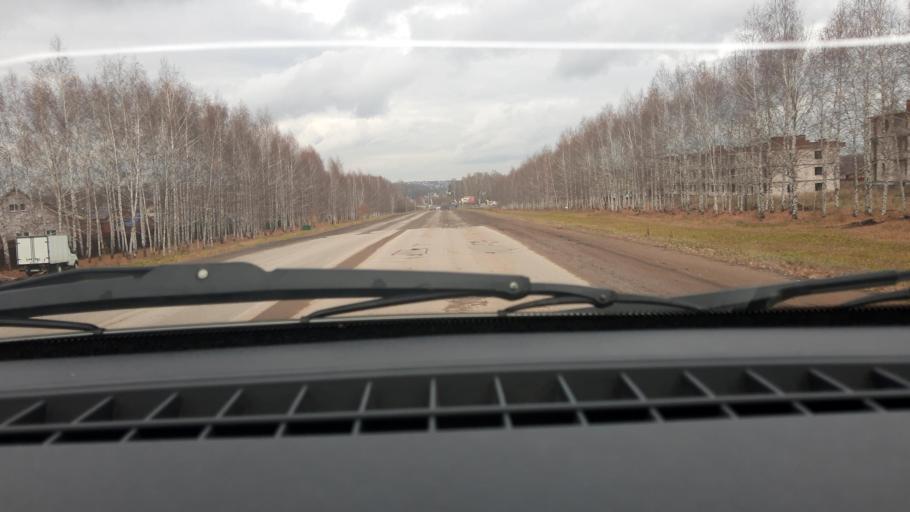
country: RU
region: Bashkortostan
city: Iglino
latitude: 54.8257
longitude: 56.4231
